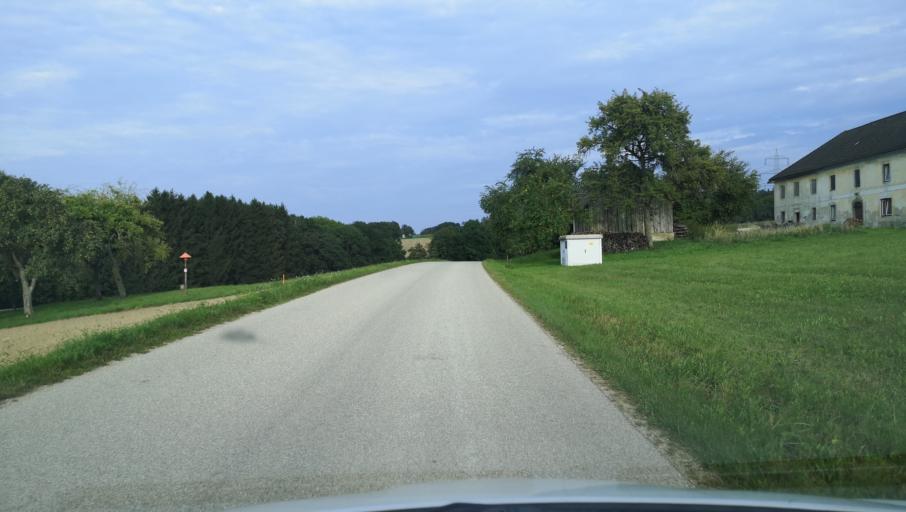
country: AT
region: Lower Austria
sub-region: Politischer Bezirk Amstetten
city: Amstetten
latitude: 48.1552
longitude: 14.8723
